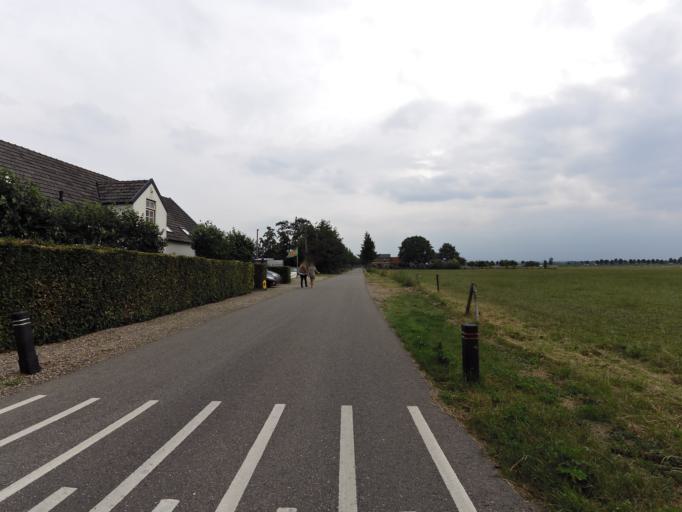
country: DE
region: North Rhine-Westphalia
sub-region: Regierungsbezirk Dusseldorf
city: Kranenburg
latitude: 51.8593
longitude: 6.0349
